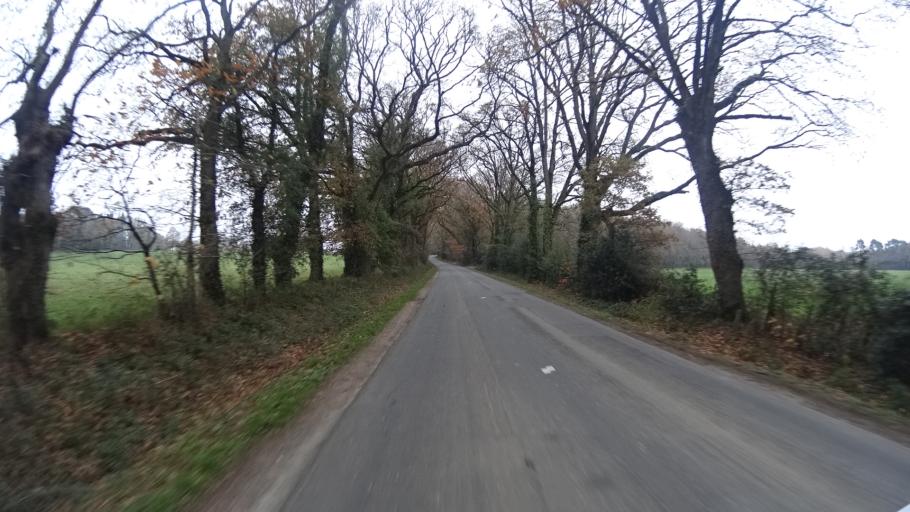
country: FR
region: Brittany
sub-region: Departement d'Ille-et-Vilaine
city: Bains-sur-Oust
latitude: 47.7012
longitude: -2.0557
